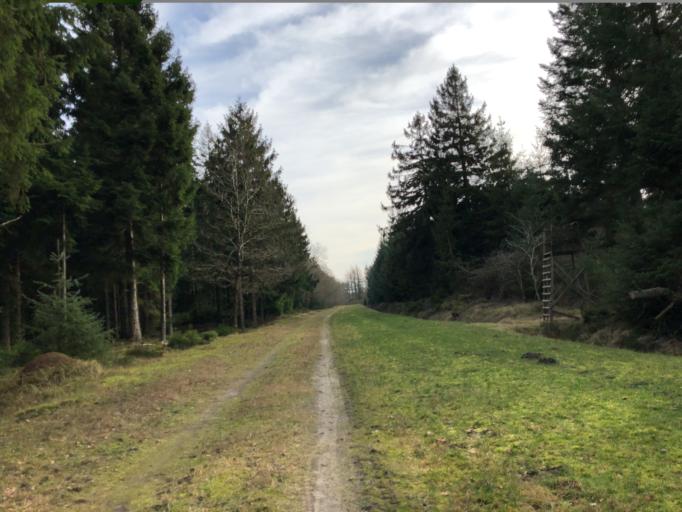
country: DK
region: Central Jutland
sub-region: Holstebro Kommune
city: Ulfborg
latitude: 56.2581
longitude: 8.3919
